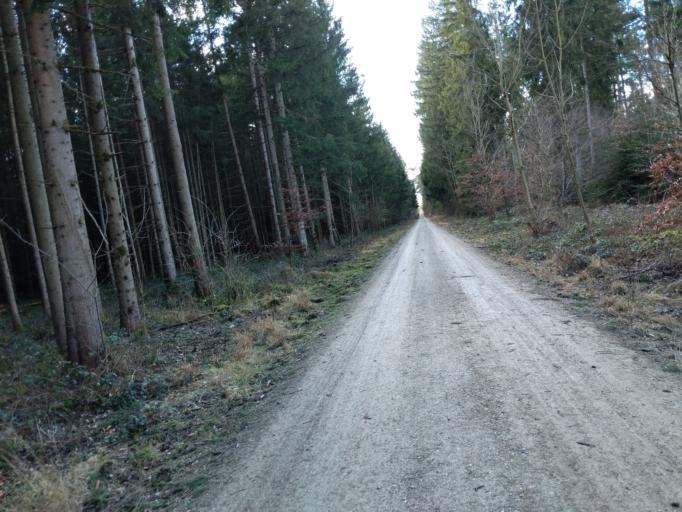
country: DE
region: Bavaria
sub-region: Upper Bavaria
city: Zorneding
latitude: 48.1007
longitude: 11.8495
